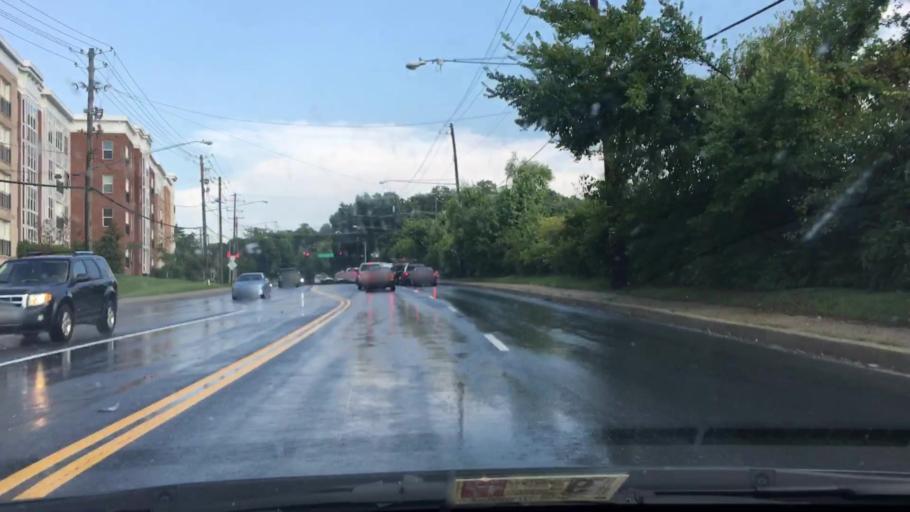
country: US
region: Maryland
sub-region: Prince George's County
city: South Laurel
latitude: 39.0608
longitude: -76.8827
